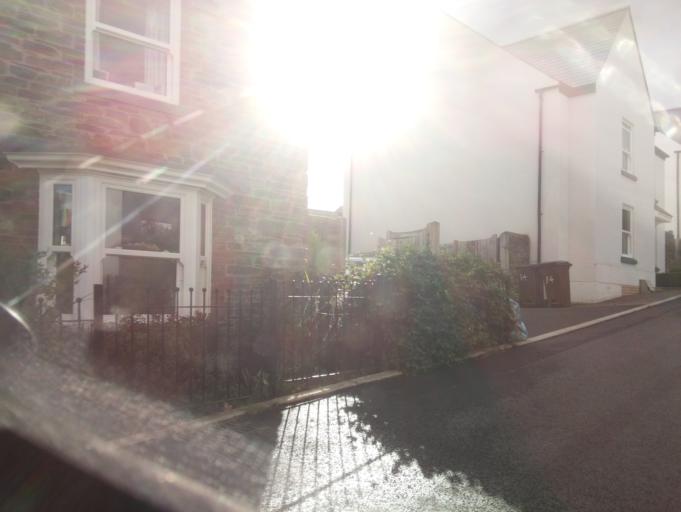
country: GB
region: England
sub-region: Devon
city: Ivybridge
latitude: 50.3631
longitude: -3.9133
